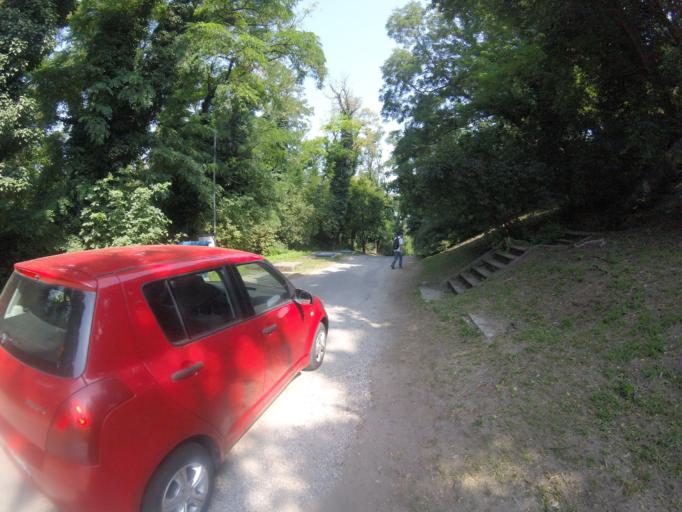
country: HU
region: Veszprem
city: Tapolca
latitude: 46.8041
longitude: 17.4342
